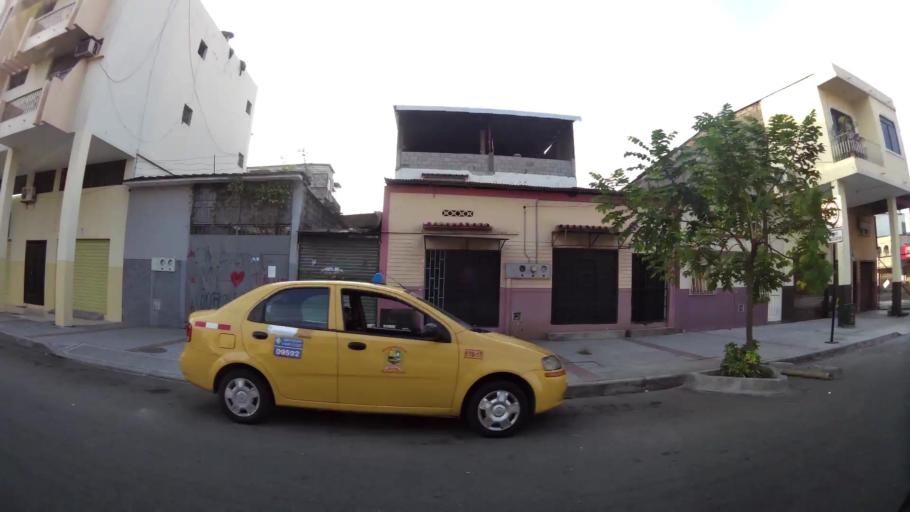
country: EC
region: Guayas
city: Guayaquil
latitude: -2.2074
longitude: -79.9000
